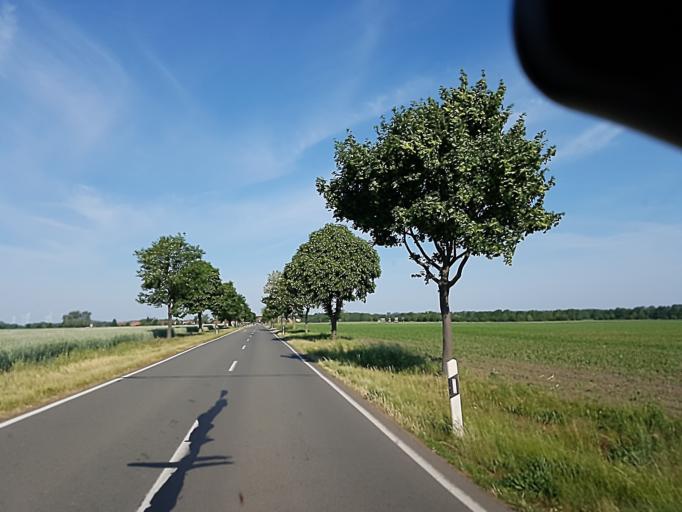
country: DE
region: Saxony-Anhalt
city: Rosslau
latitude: 52.0111
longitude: 12.2476
